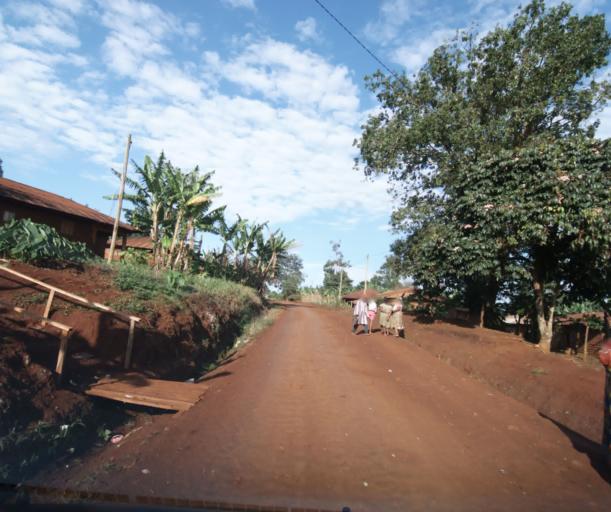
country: CM
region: West
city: Mbouda
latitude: 5.6207
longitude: 10.3206
